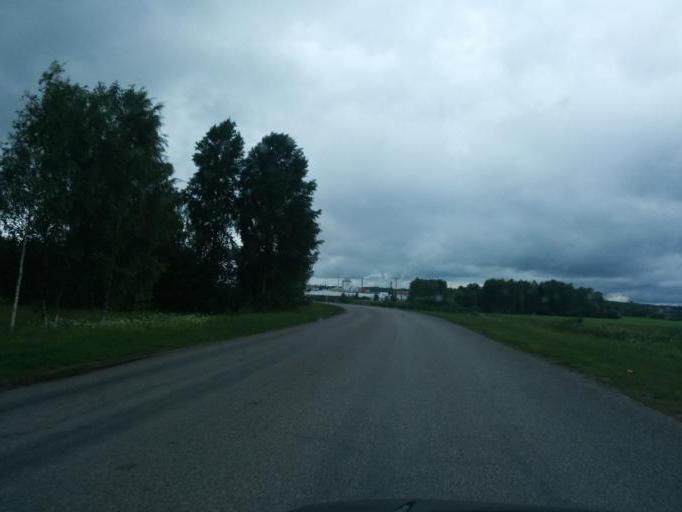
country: LV
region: Valmieras Rajons
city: Valmiera
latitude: 57.5144
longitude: 25.4548
